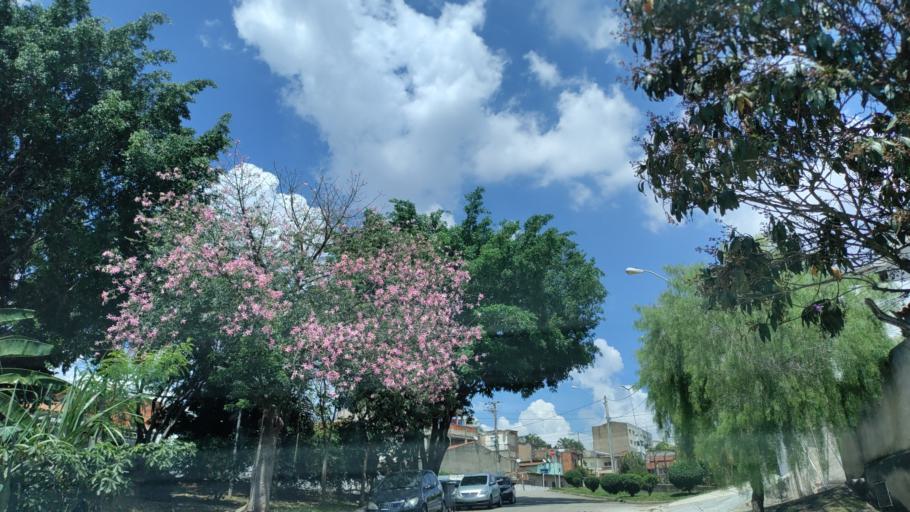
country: BR
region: Sao Paulo
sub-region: Sorocaba
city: Sorocaba
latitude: -23.4851
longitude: -47.4626
